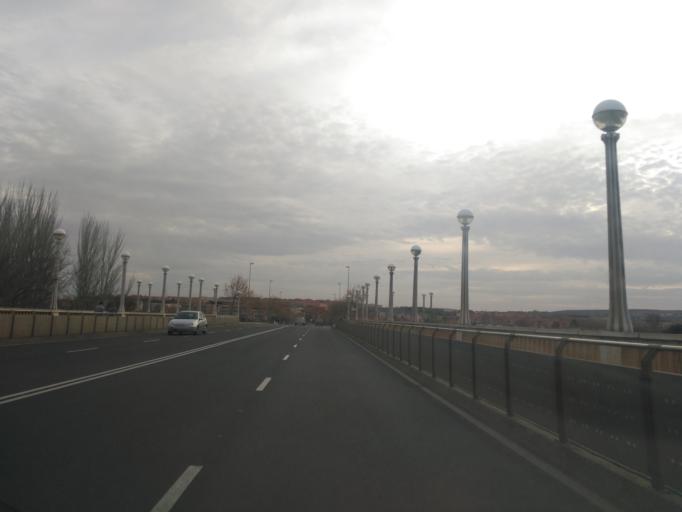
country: ES
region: Castille and Leon
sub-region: Provincia de Salamanca
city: Salamanca
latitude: 40.9625
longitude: -5.6809
